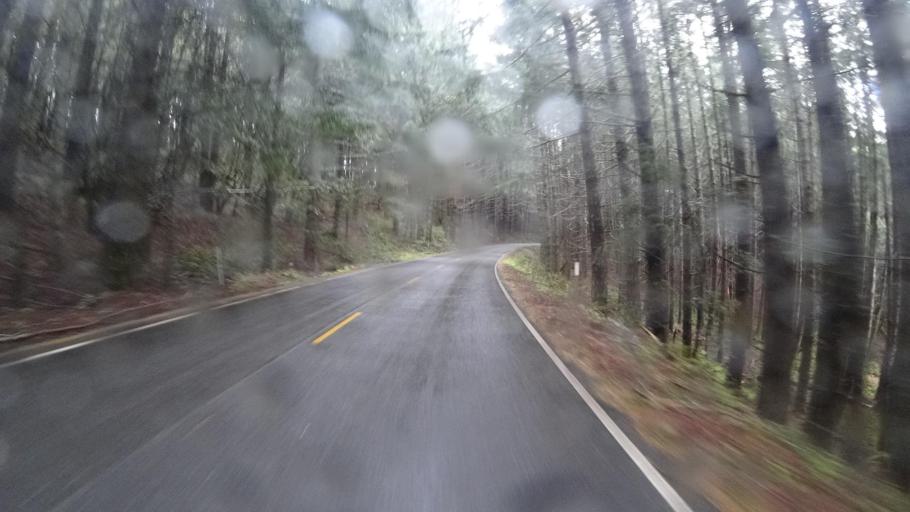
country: US
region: California
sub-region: Humboldt County
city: Westhaven-Moonstone
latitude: 41.2180
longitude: -123.9575
